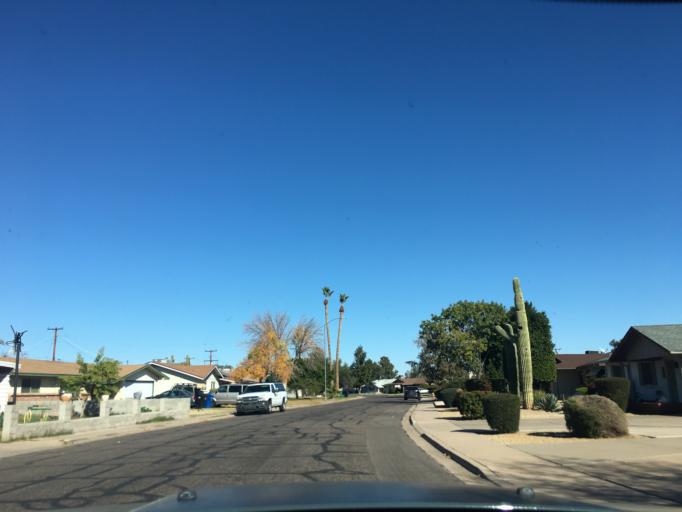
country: US
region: Arizona
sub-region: Maricopa County
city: Mesa
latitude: 33.4455
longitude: -111.8498
